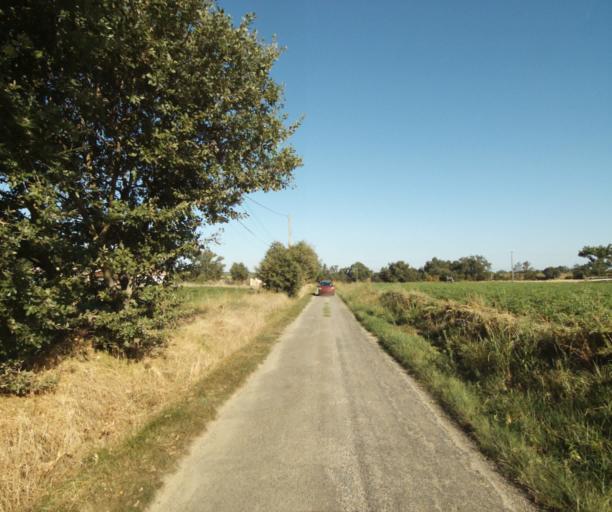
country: FR
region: Midi-Pyrenees
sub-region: Departement du Tarn-et-Garonne
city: Verdun-sur-Garonne
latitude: 43.8597
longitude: 1.2164
